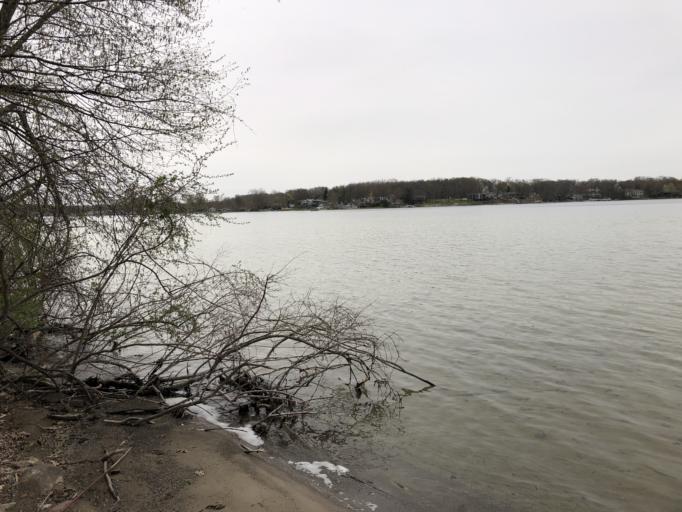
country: US
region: Indiana
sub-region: Steuben County
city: Angola
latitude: 41.7138
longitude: -85.0348
